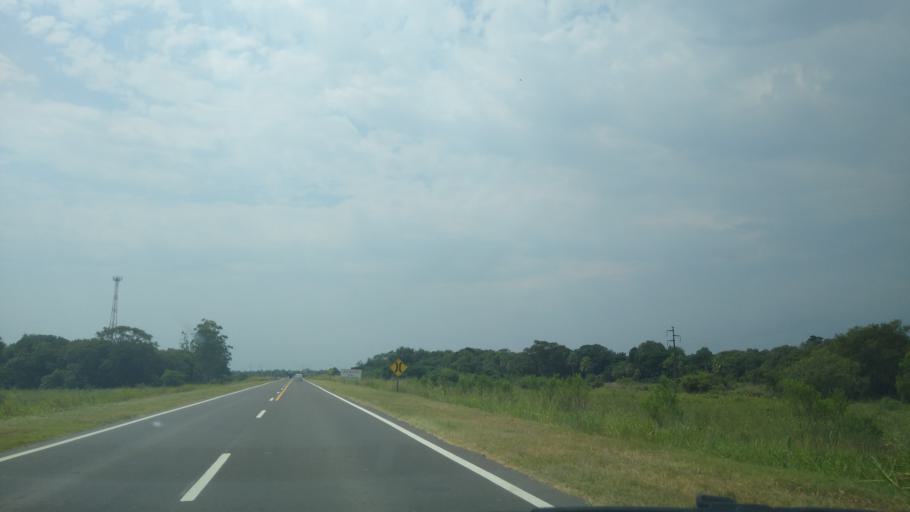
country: AR
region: Chaco
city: Margarita Belen
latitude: -27.0949
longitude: -58.9607
